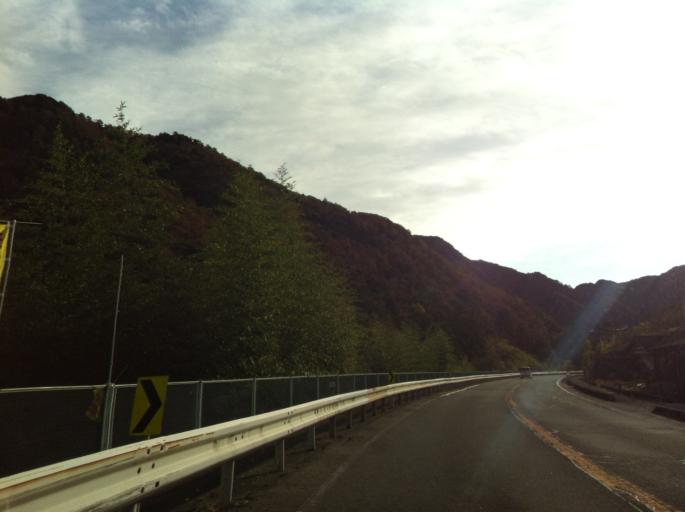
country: JP
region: Gifu
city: Mitake
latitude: 35.5479
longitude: 137.1528
